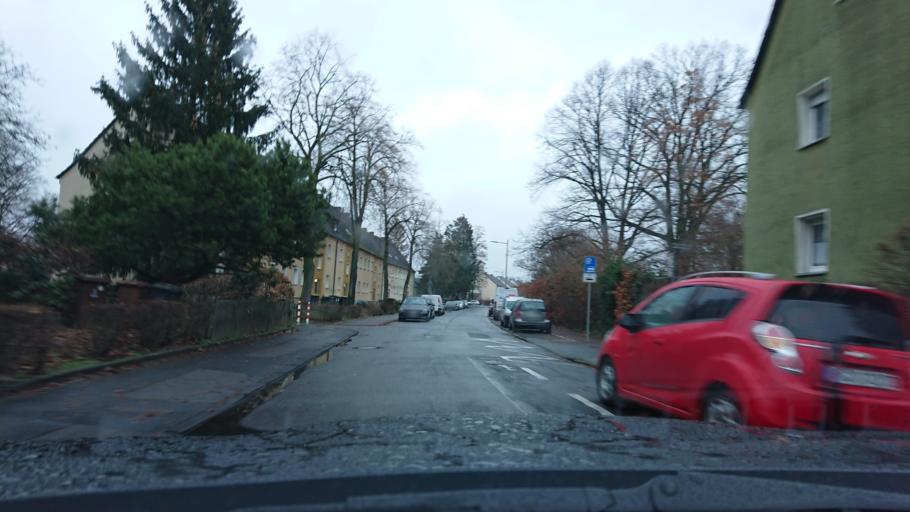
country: DE
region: North Rhine-Westphalia
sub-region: Regierungsbezirk Koln
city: Siegburg
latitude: 50.8069
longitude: 7.1897
